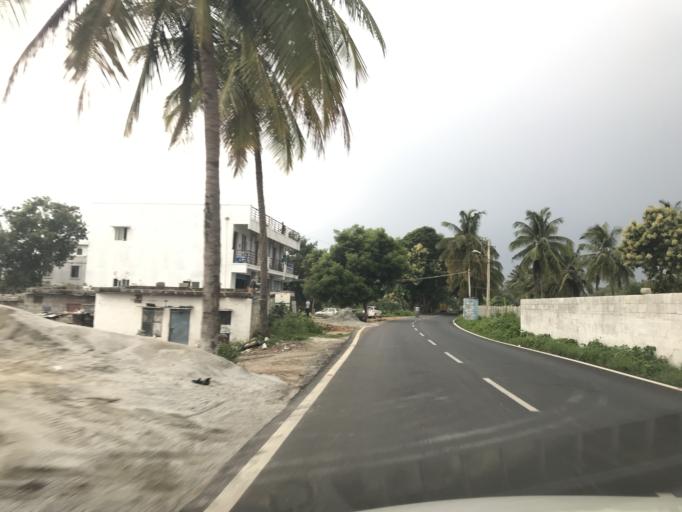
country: IN
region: Karnataka
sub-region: Bangalore Urban
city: Yelahanka
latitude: 13.1786
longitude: 77.6485
